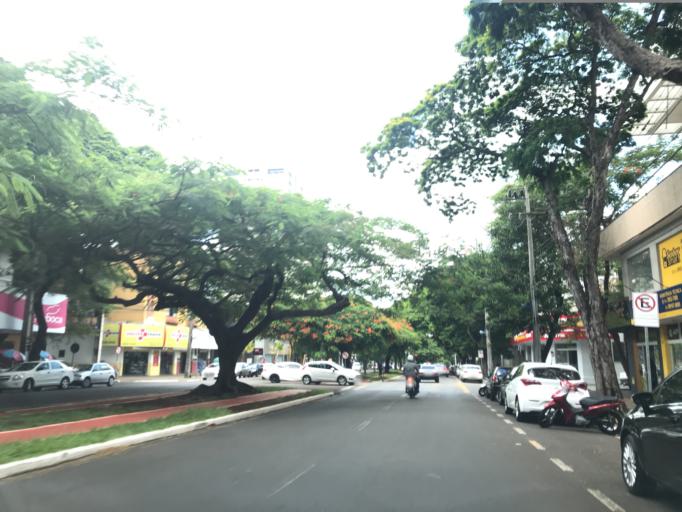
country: BR
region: Parana
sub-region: Maringa
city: Maringa
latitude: -23.4165
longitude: -51.9269
